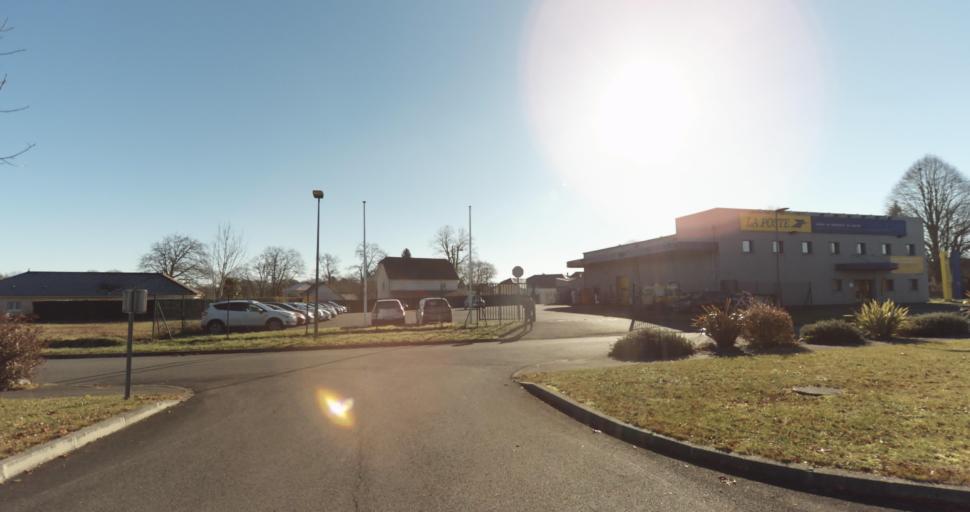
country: FR
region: Aquitaine
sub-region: Departement des Pyrenees-Atlantiques
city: Morlaas
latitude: 43.3387
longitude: -0.2509
